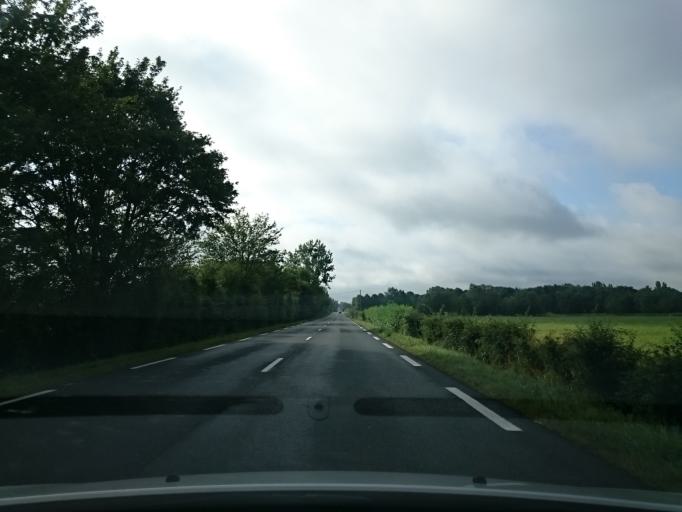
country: FR
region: Lower Normandy
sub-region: Departement du Calvados
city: Cambremer
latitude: 49.1293
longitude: 0.0031
